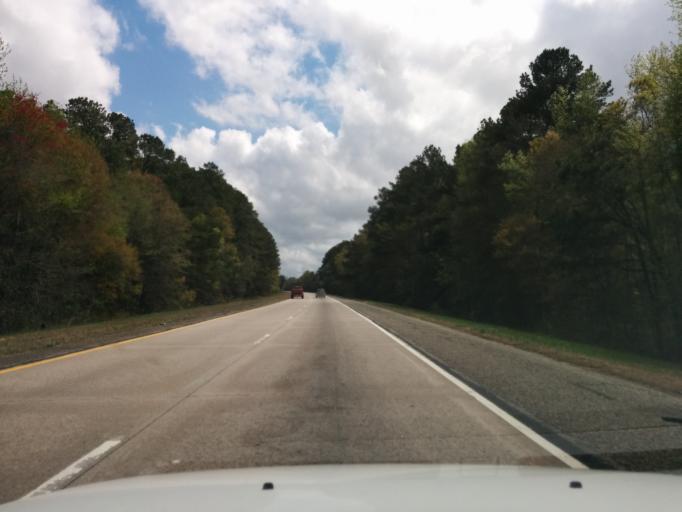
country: US
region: Georgia
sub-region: Bryan County
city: Pembroke
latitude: 32.2470
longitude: -81.6933
